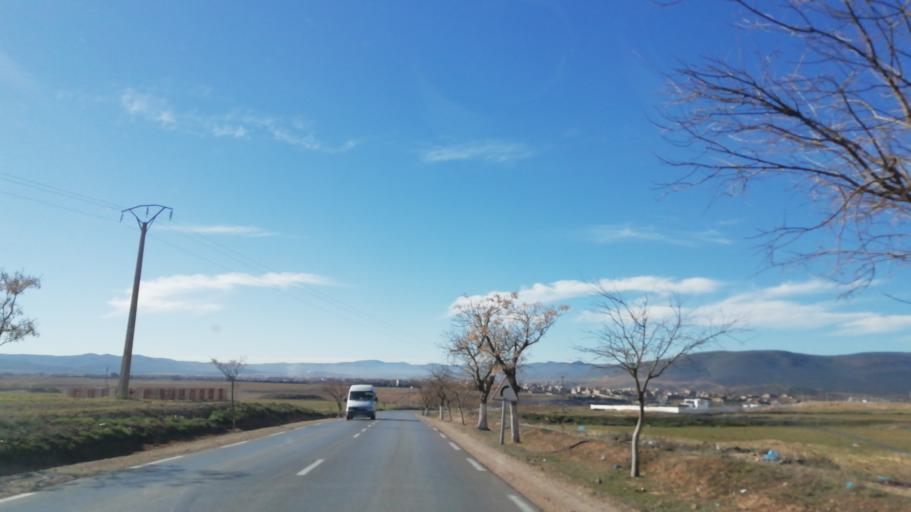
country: DZ
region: Tlemcen
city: Sebdou
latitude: 34.6586
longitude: -1.2995
